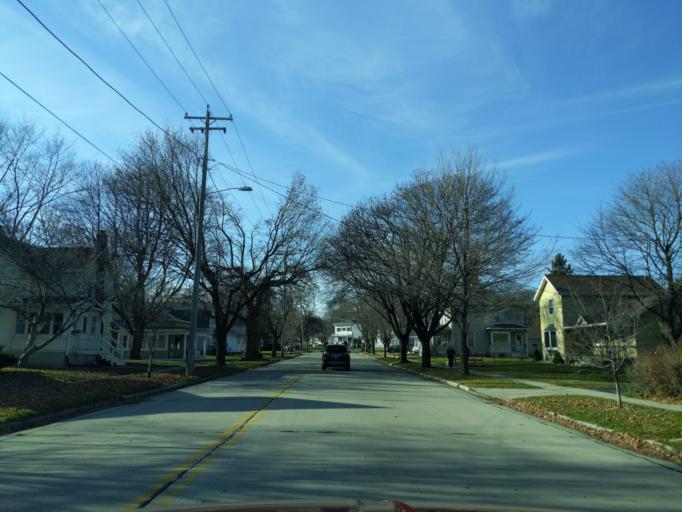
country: US
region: Wisconsin
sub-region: Walworth County
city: Whitewater
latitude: 42.8302
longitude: -88.7380
